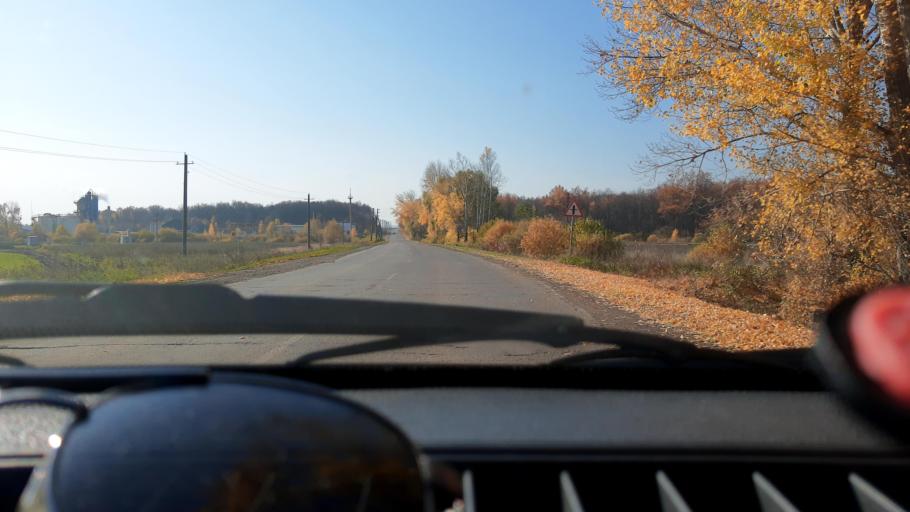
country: RU
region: Bashkortostan
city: Mikhaylovka
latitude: 54.8490
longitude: 55.8467
